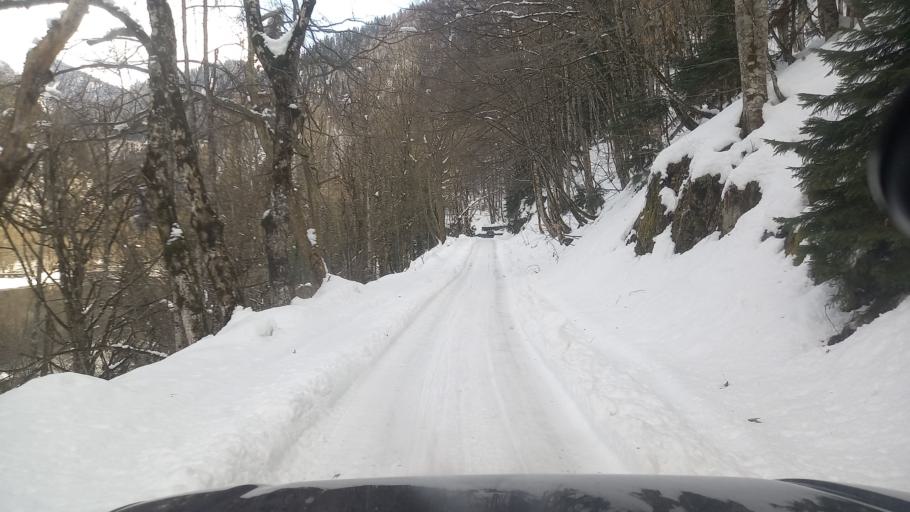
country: GE
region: Abkhazia
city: Gagra
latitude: 43.4790
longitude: 40.5548
